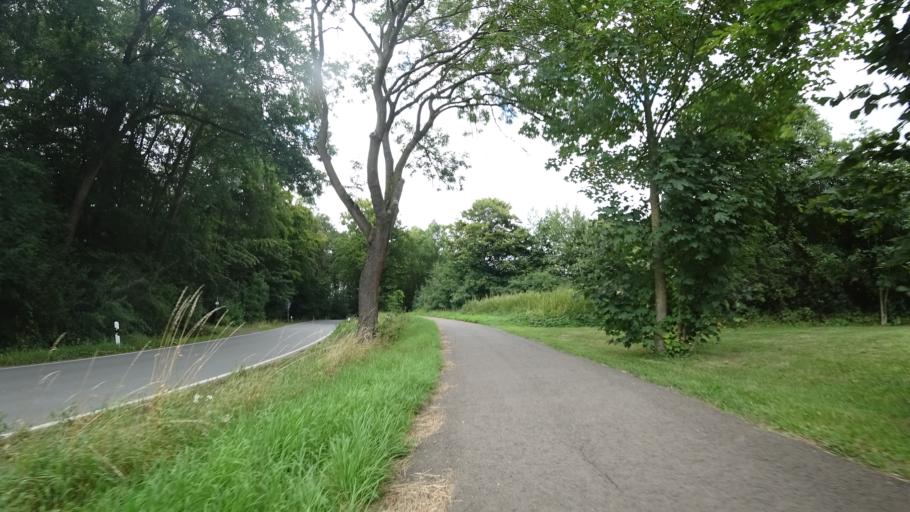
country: DE
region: Lower Saxony
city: Leese
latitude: 52.4692
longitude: 9.0884
